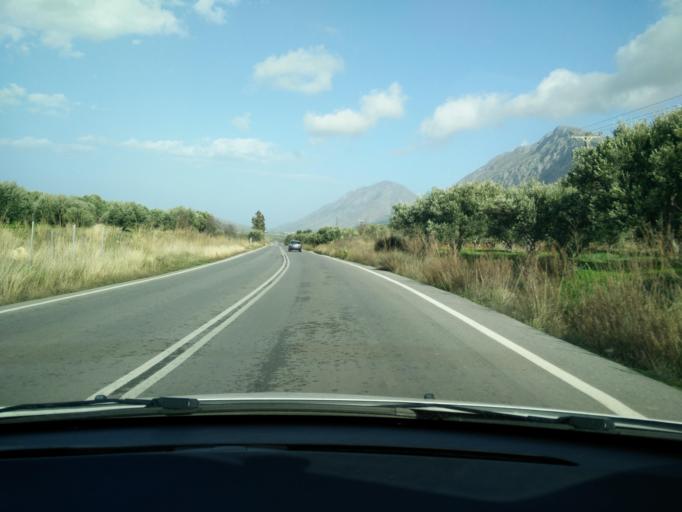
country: GR
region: Crete
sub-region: Nomos Lasithiou
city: Kato Chorio
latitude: 35.0714
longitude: 25.8055
